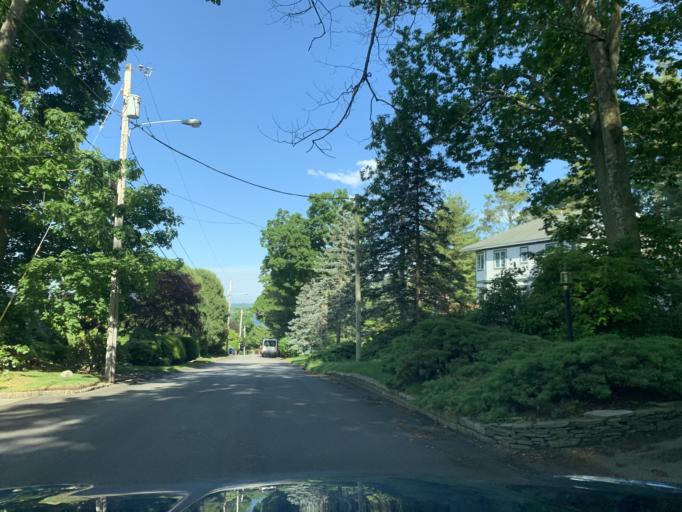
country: US
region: Rhode Island
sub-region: Kent County
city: East Greenwich
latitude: 41.6826
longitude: -71.4545
